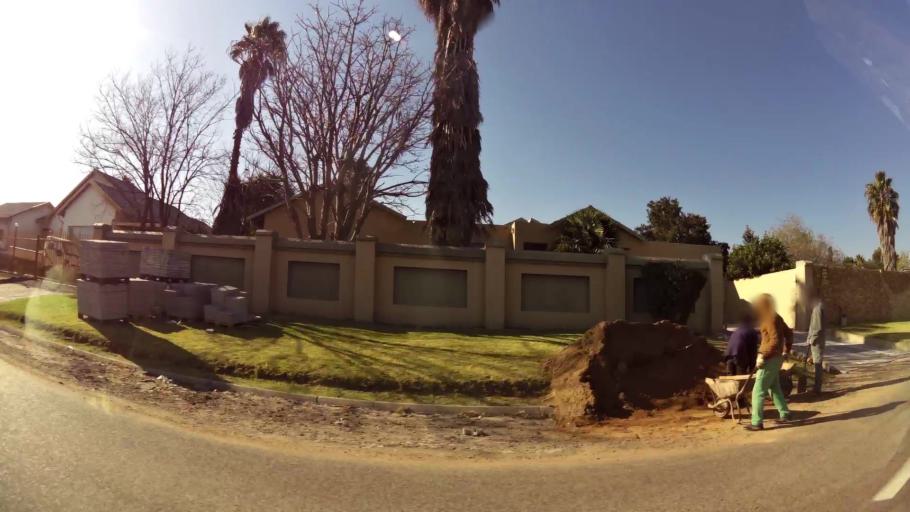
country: ZA
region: Gauteng
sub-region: City of Johannesburg Metropolitan Municipality
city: Modderfontein
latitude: -26.0628
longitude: 28.1980
